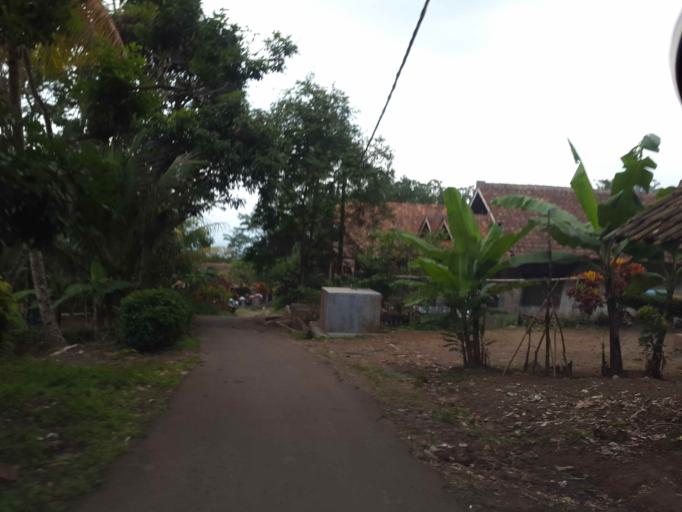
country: ID
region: Banten
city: Campraksanta
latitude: -6.3071
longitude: 106.0734
